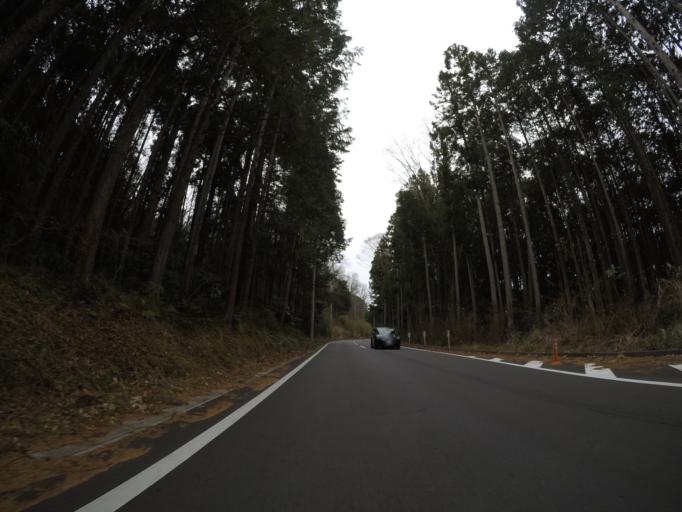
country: JP
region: Shizuoka
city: Fujinomiya
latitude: 35.2418
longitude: 138.5717
